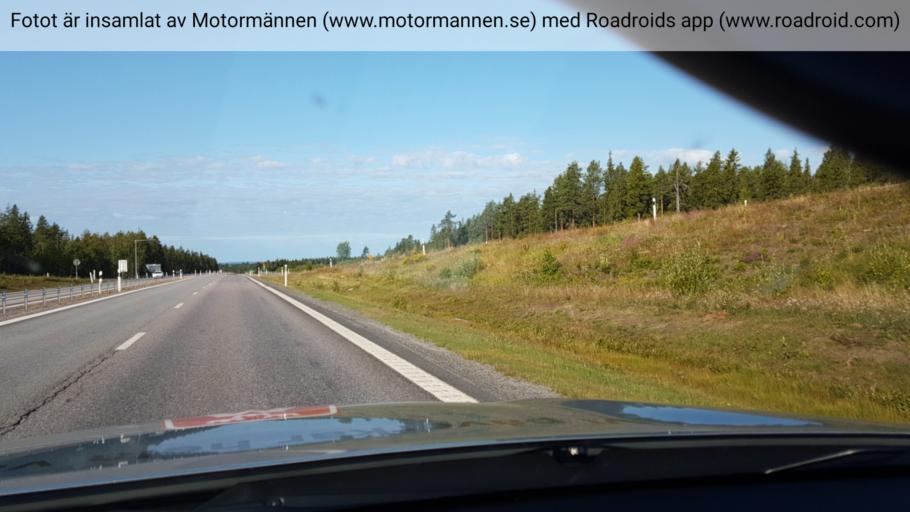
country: SE
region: Norrbotten
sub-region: Lulea Kommun
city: Sodra Sunderbyn
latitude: 65.5743
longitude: 21.9376
